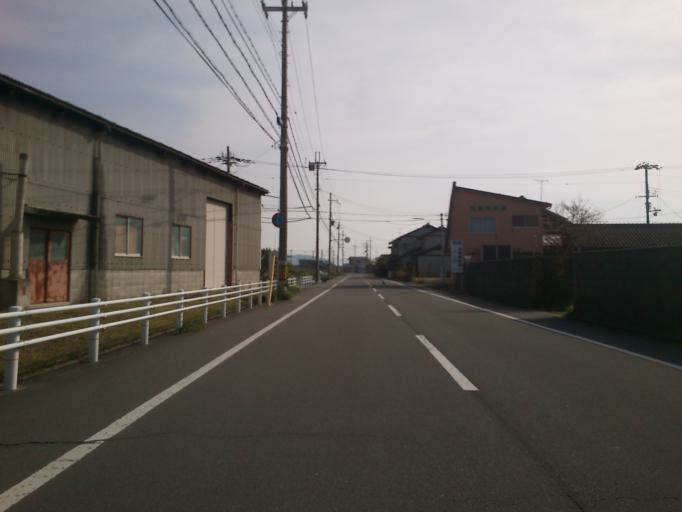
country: JP
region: Kyoto
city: Miyazu
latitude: 35.5831
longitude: 135.2034
